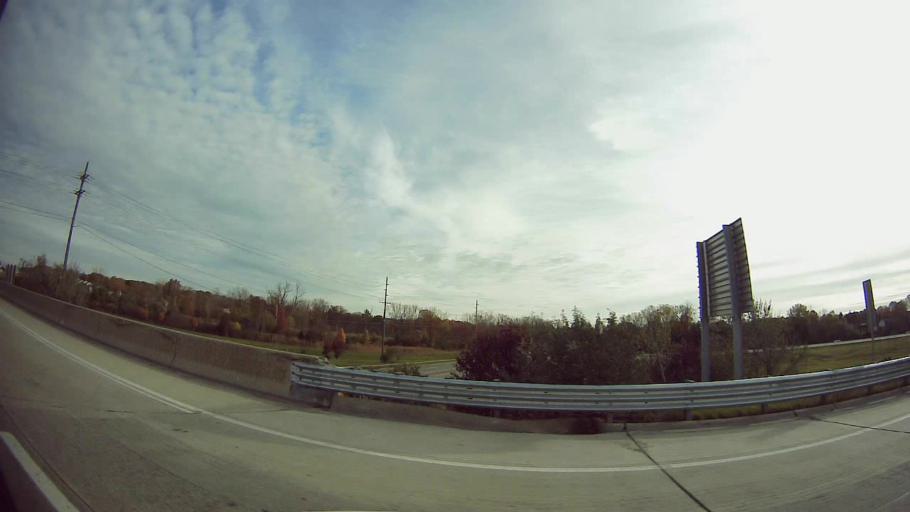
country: US
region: Michigan
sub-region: Wayne County
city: Northville
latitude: 42.4387
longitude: -83.4316
